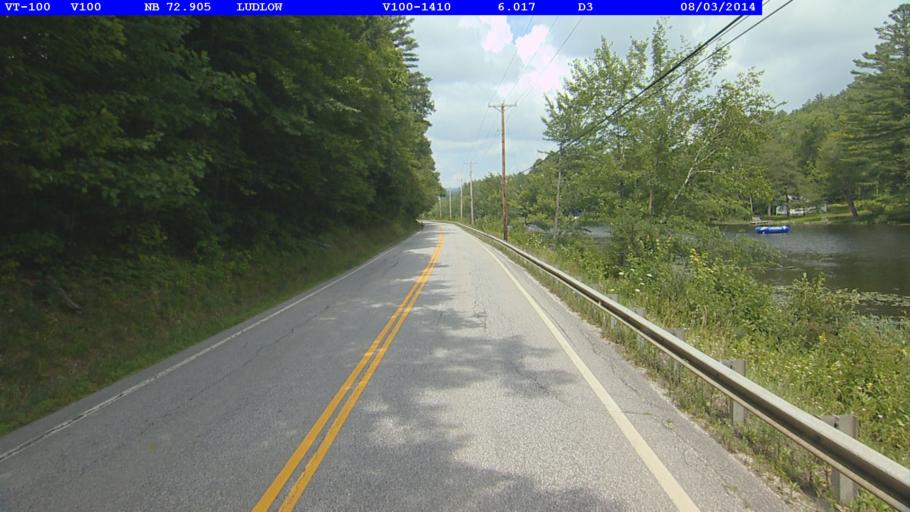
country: US
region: Vermont
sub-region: Windsor County
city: Chester
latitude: 43.4320
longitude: -72.6982
